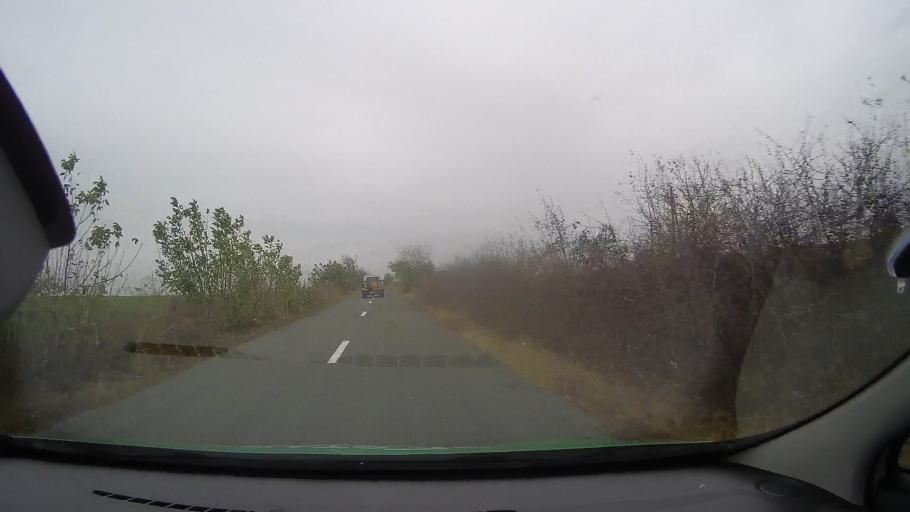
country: RO
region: Constanta
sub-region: Comuna Targusor
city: Targusor
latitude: 44.4759
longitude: 28.3802
